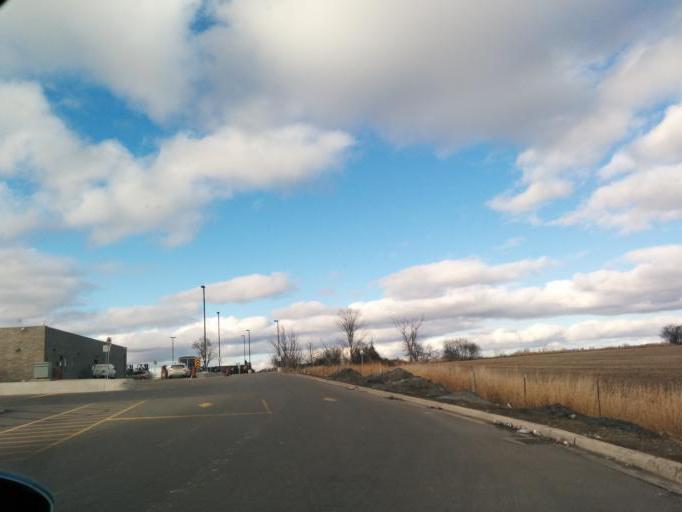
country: CA
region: Ontario
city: Vaughan
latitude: 43.8943
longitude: -79.5567
